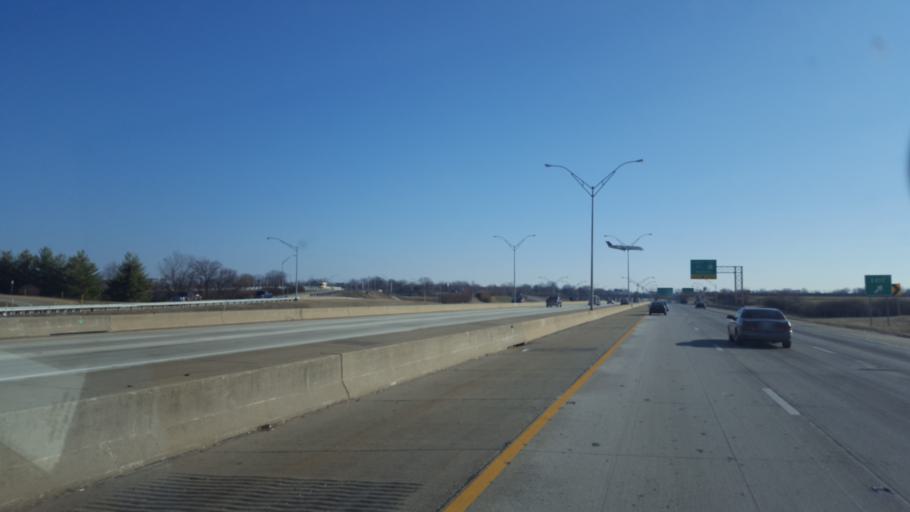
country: US
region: Kentucky
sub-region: Jefferson County
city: Audubon Park
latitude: 38.1896
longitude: -85.7379
